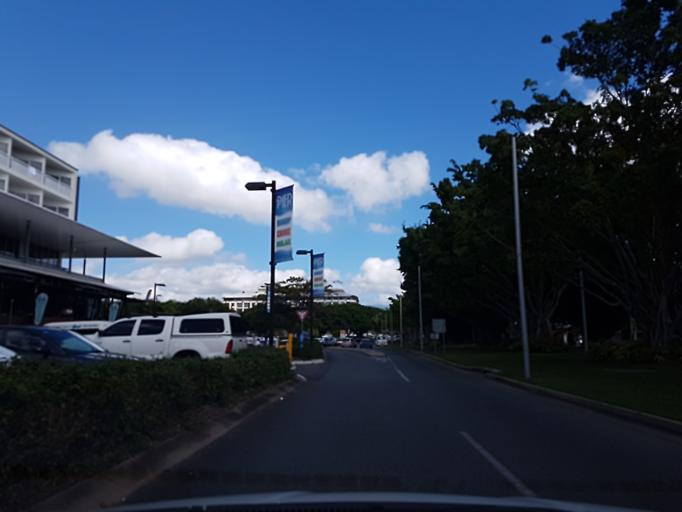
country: AU
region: Queensland
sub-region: Cairns
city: Cairns
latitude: -16.9191
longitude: 145.7798
